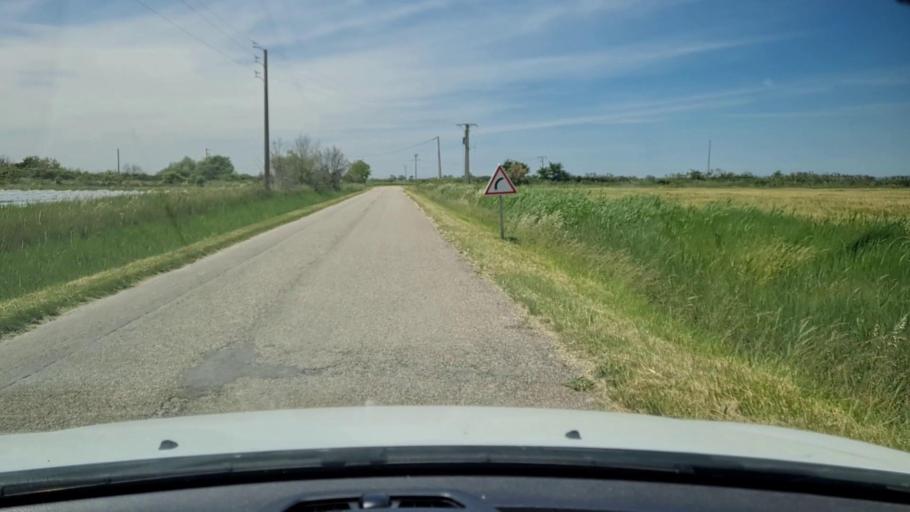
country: FR
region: Languedoc-Roussillon
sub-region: Departement du Gard
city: Saint-Gilles
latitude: 43.6096
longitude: 4.4283
